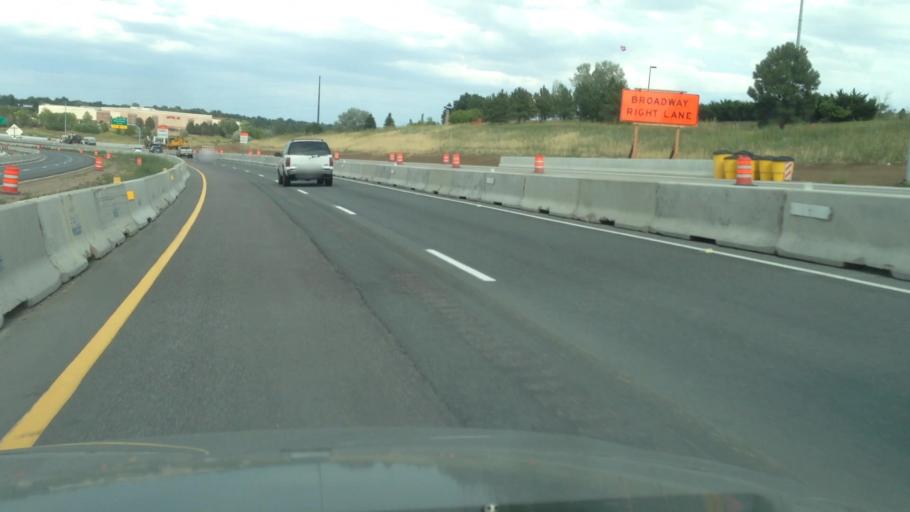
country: US
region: Colorado
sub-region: Douglas County
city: Highlands Ranch
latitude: 39.5587
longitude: -105.0013
